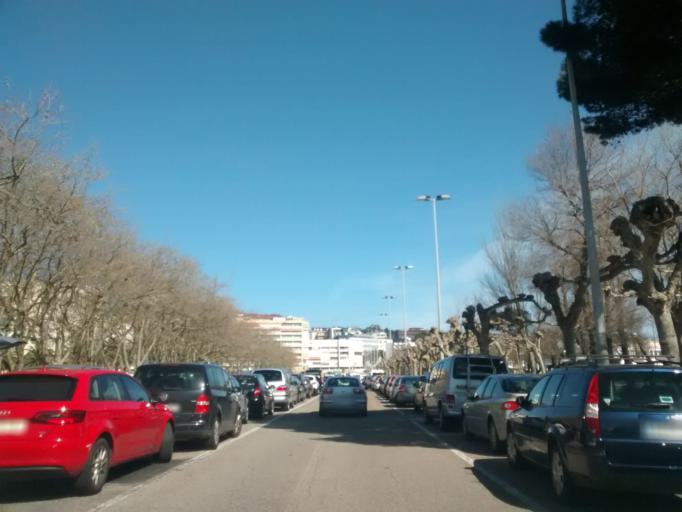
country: ES
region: Cantabria
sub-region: Provincia de Cantabria
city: Santander
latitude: 43.4764
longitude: -3.7886
